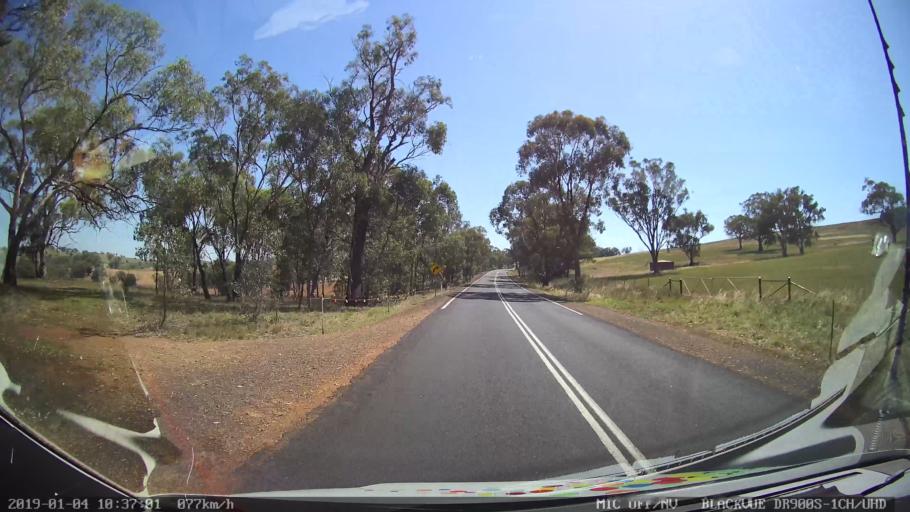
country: AU
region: New South Wales
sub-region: Cabonne
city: Canowindra
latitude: -33.2990
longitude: 148.6901
